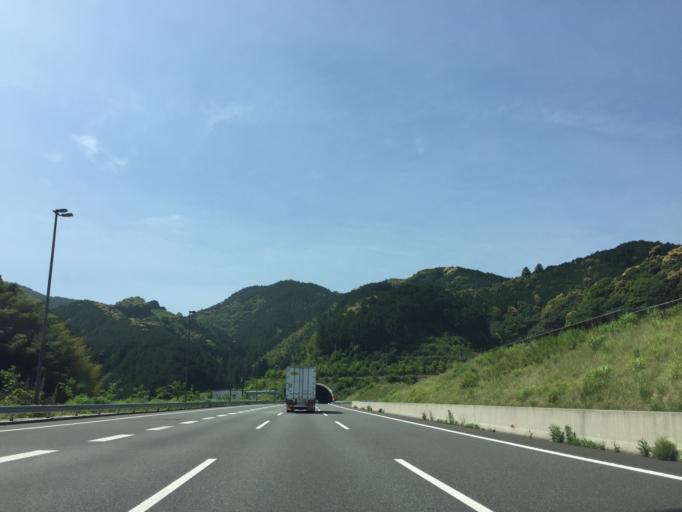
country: JP
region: Shizuoka
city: Shizuoka-shi
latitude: 34.9660
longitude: 138.2913
